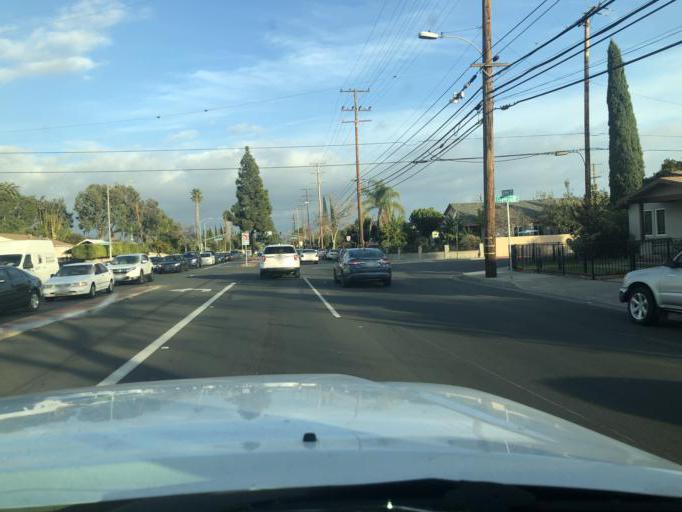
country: US
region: California
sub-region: Orange County
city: Santa Ana
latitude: 33.7272
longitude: -117.8670
